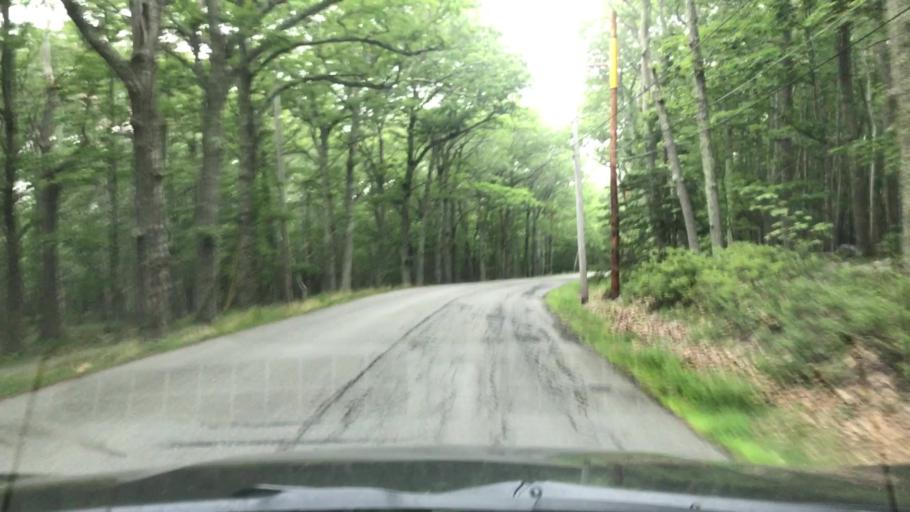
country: US
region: Maine
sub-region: Hancock County
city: Bar Harbor
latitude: 44.3464
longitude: -68.1809
